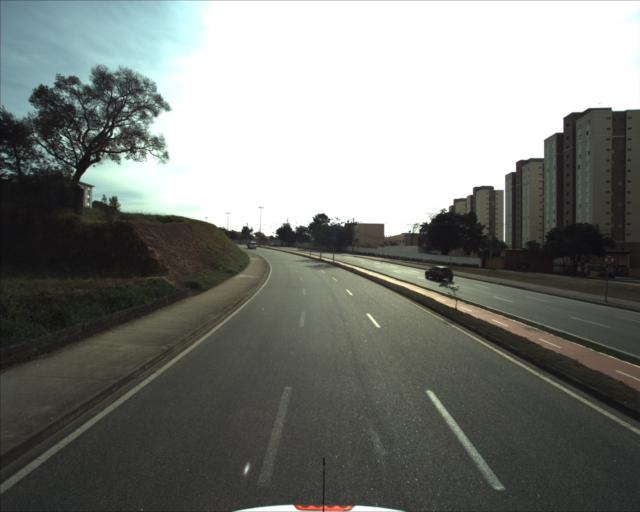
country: BR
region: Sao Paulo
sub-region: Sorocaba
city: Sorocaba
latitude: -23.4779
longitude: -47.4555
